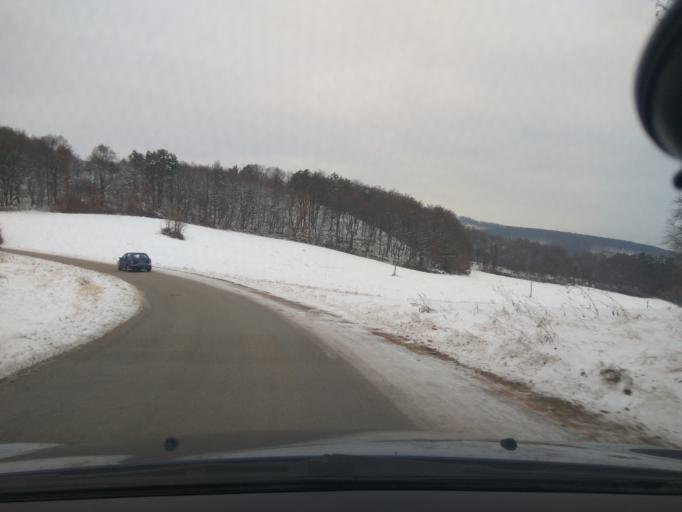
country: SK
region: Nitriansky
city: Stara Tura
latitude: 48.8292
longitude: 17.7080
